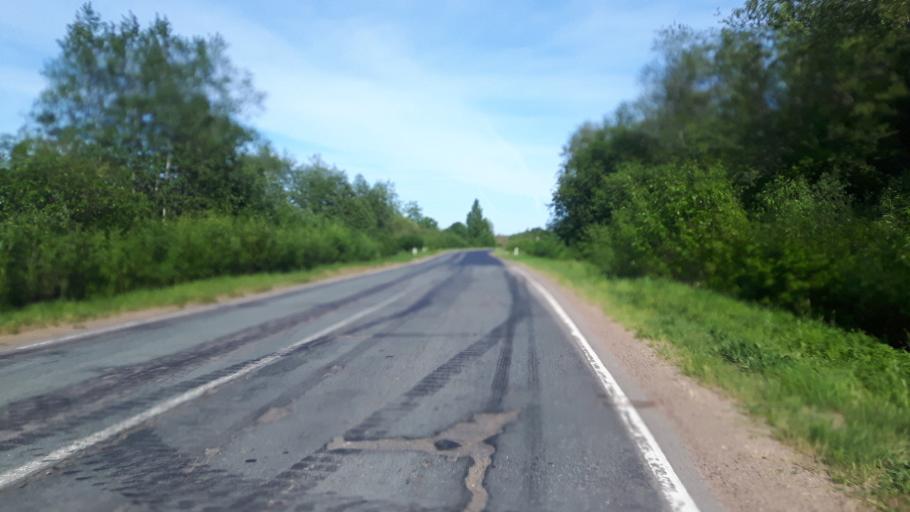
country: RU
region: Leningrad
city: Ivangorod
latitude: 59.4163
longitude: 28.3728
